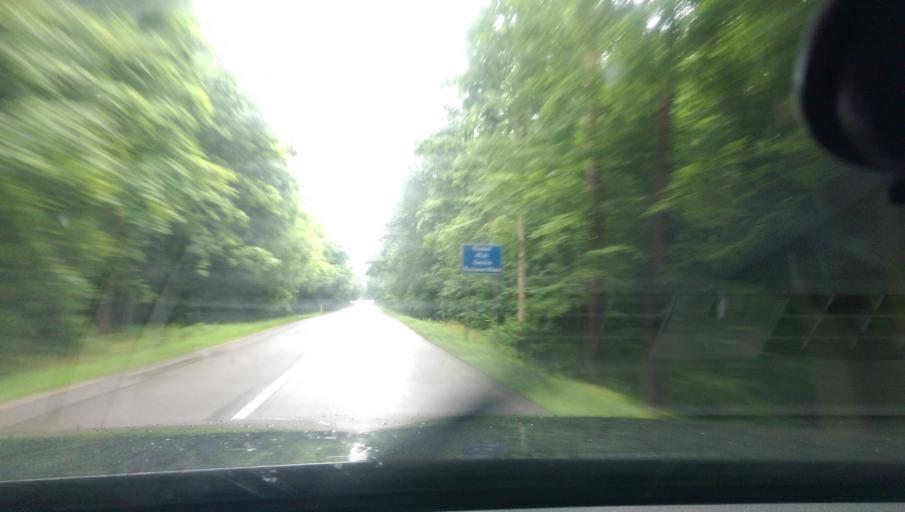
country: PL
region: Warmian-Masurian Voivodeship
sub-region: Powiat piski
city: Ruciane-Nida
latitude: 53.7007
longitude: 21.4644
